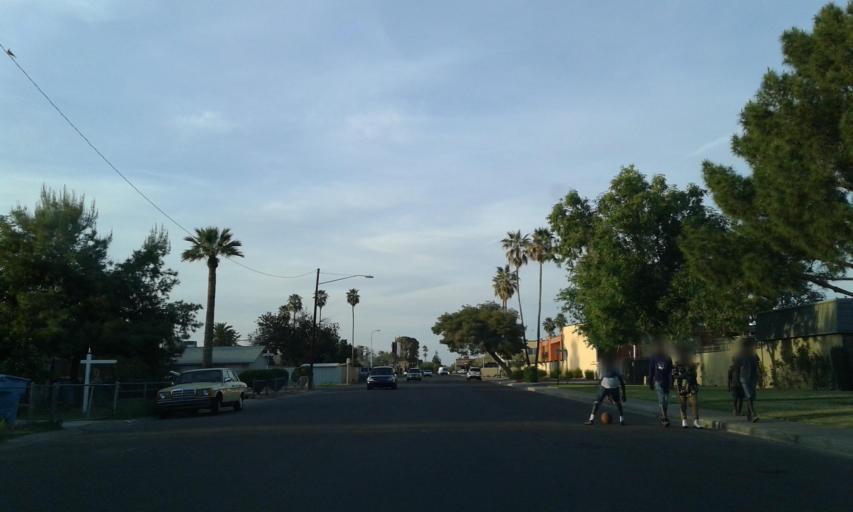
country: US
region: Arizona
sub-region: Maricopa County
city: Phoenix
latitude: 33.5071
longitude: -112.1042
